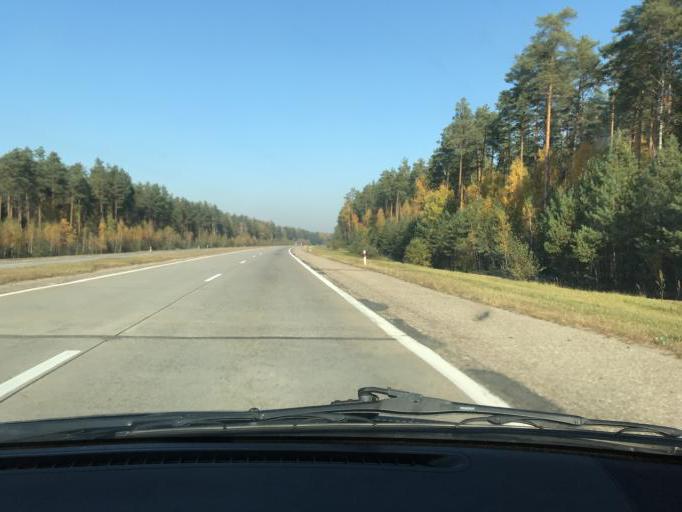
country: BY
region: Minsk
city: Uzda
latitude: 53.3996
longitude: 27.4812
